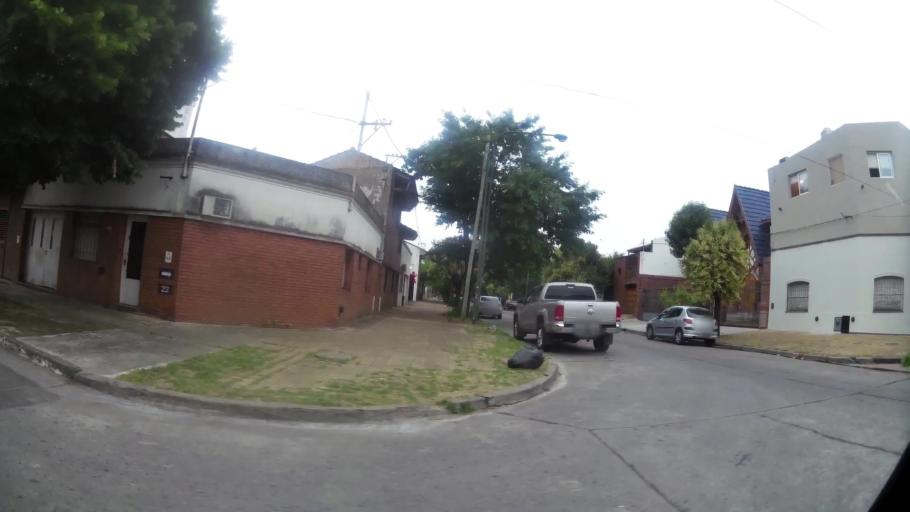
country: AR
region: Buenos Aires
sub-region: Partido de La Plata
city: La Plata
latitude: -34.9180
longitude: -57.9798
